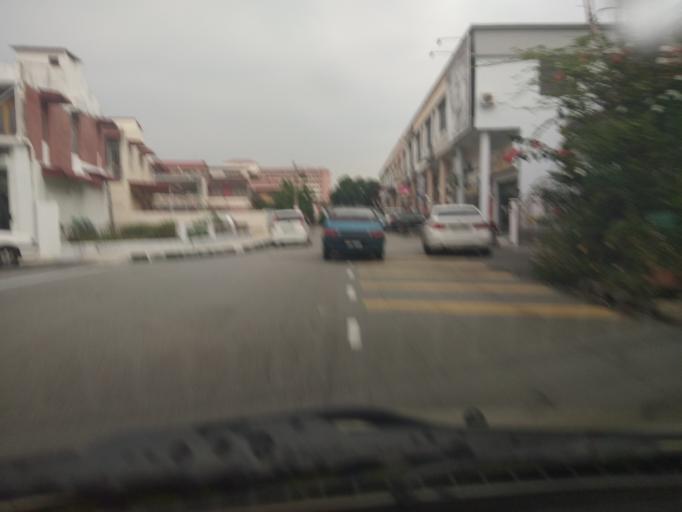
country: MY
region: Penang
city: Permatang Kuching
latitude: 5.4360
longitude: 100.3811
